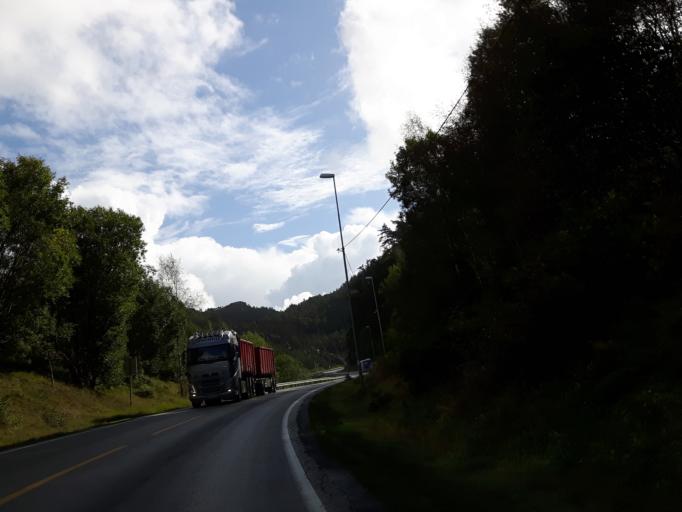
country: NO
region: Vest-Agder
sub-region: Flekkefjord
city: Flekkefjord
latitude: 58.2812
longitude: 6.7122
